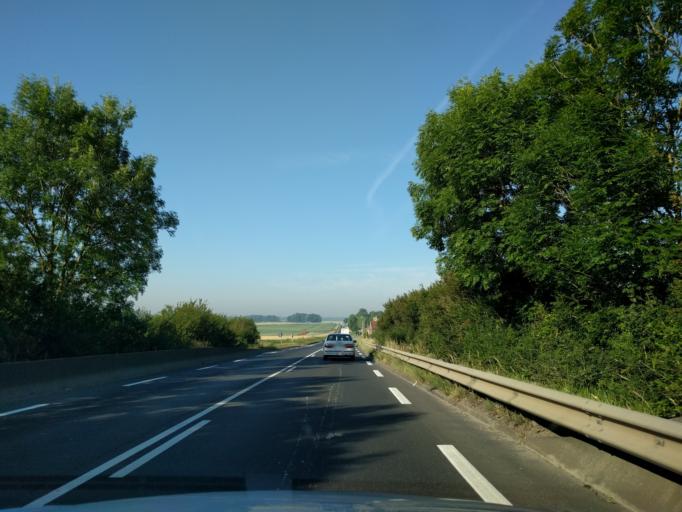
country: FR
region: Picardie
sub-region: Departement de la Somme
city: Roye
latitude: 49.6772
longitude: 2.7700
